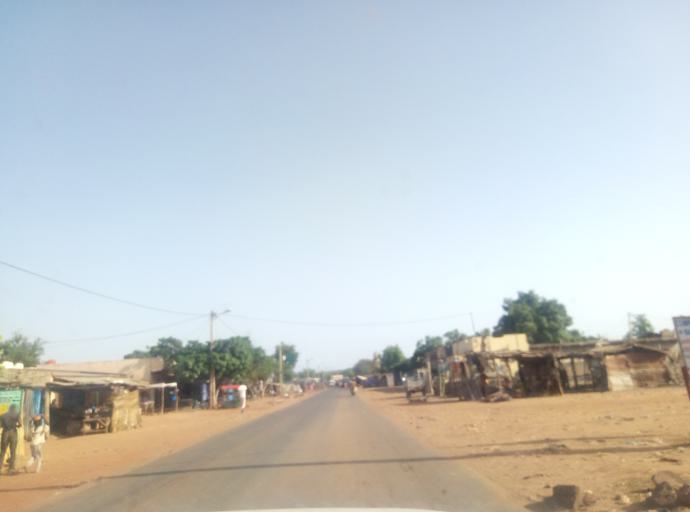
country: ML
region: Bamako
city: Bamako
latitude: 12.5898
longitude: -7.7665
